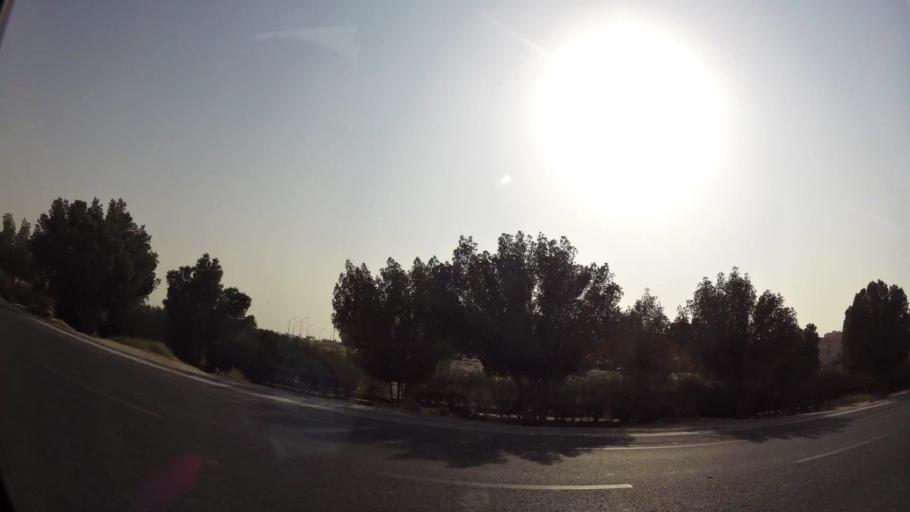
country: KW
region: Muhafazat al Jahra'
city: Al Jahra'
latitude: 29.3262
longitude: 47.7449
